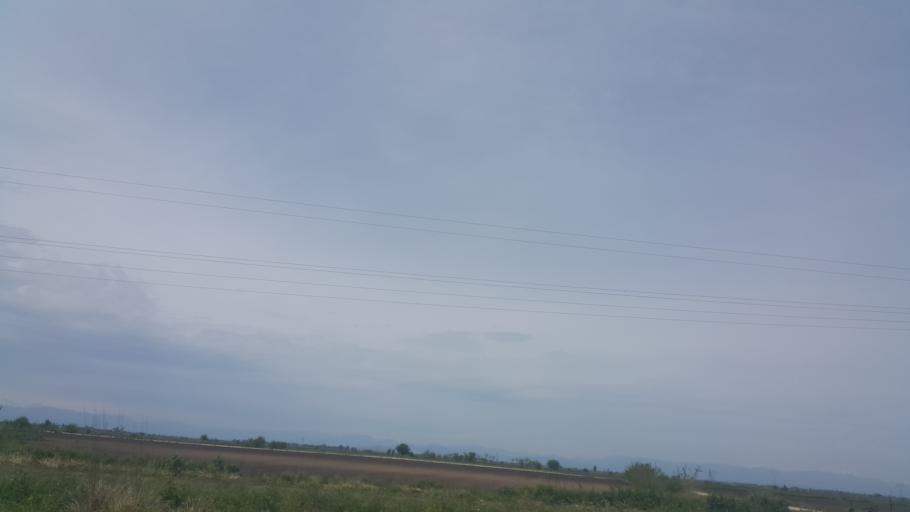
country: TR
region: Adana
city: Kosreli
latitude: 37.0636
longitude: 35.9485
